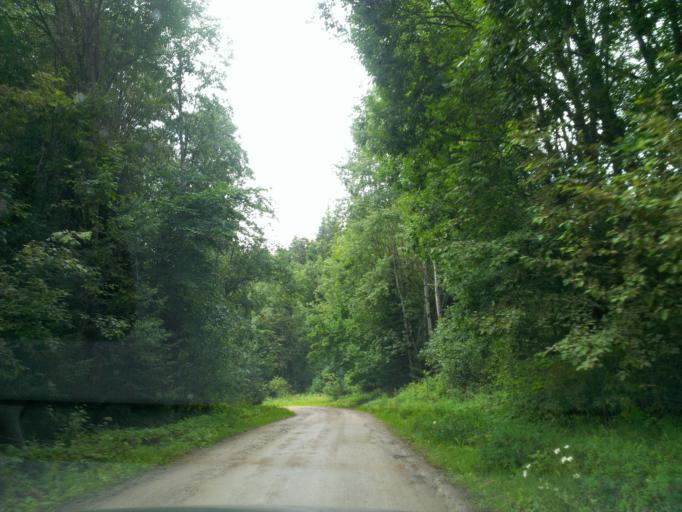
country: LV
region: Ligatne
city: Ligatne
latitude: 57.2245
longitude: 24.9851
